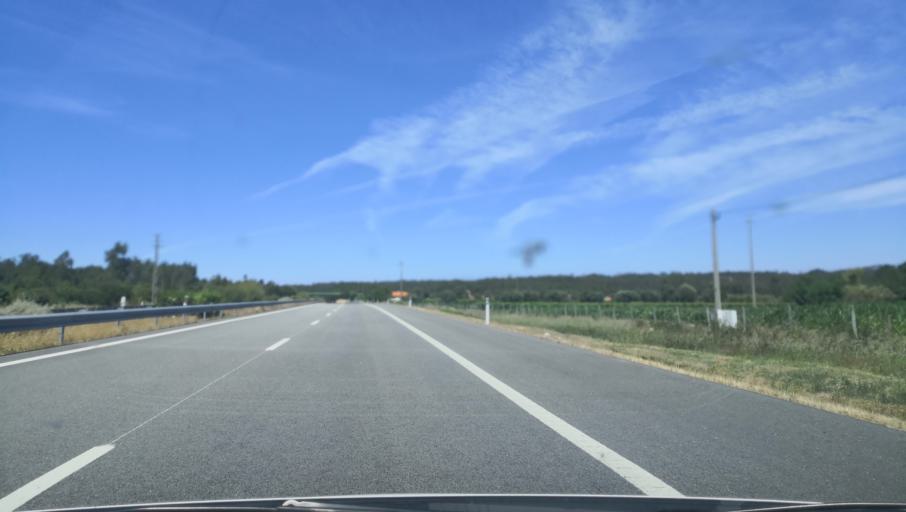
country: PT
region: Coimbra
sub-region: Montemor-O-Velho
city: Arazede
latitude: 40.2332
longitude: -8.6649
